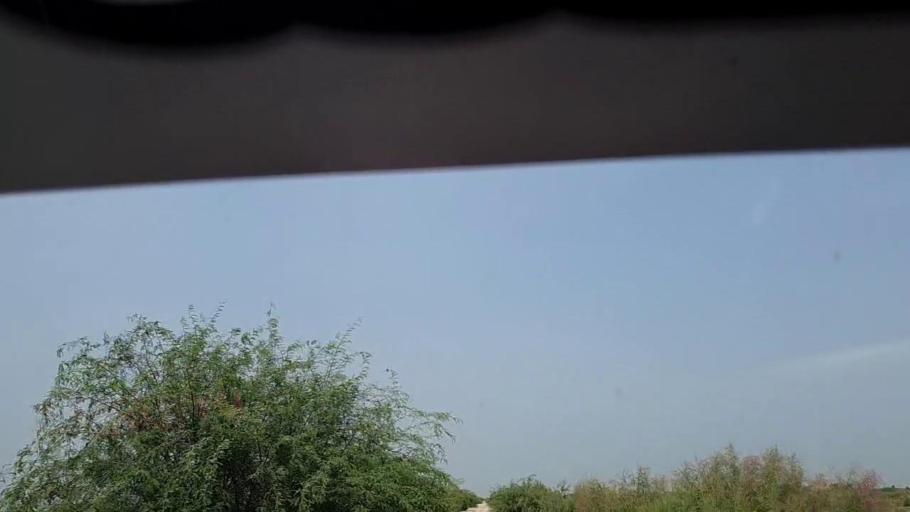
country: PK
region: Sindh
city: Adilpur
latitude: 27.8874
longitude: 69.2567
